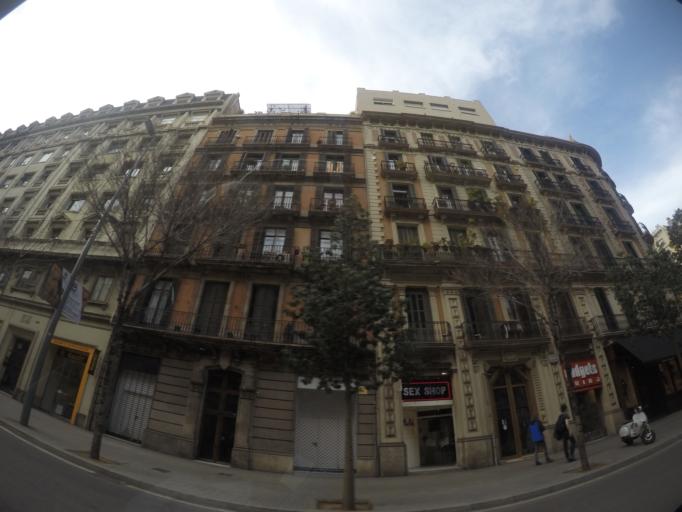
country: ES
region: Catalonia
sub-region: Provincia de Barcelona
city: Eixample
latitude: 41.3909
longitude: 2.1632
